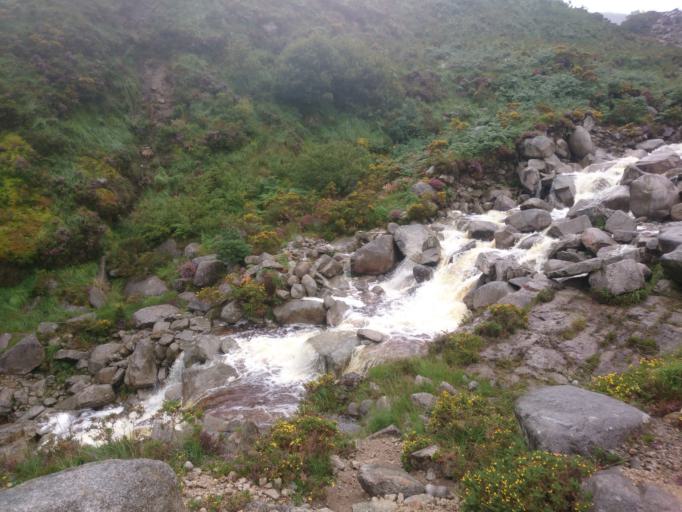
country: GB
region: Northern Ireland
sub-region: Down District
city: Newcastle
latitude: 54.1730
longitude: -5.8899
